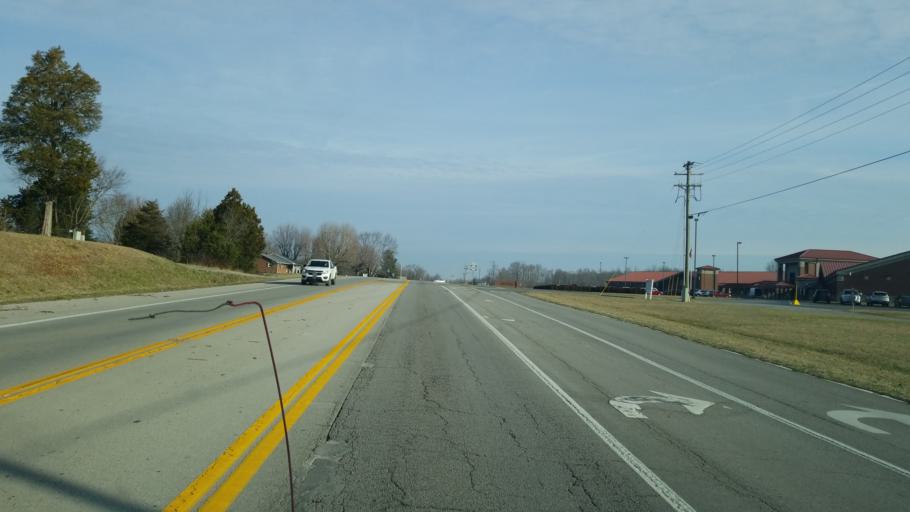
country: US
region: Kentucky
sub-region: Russell County
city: Russell Springs
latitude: 37.0865
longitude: -85.0669
